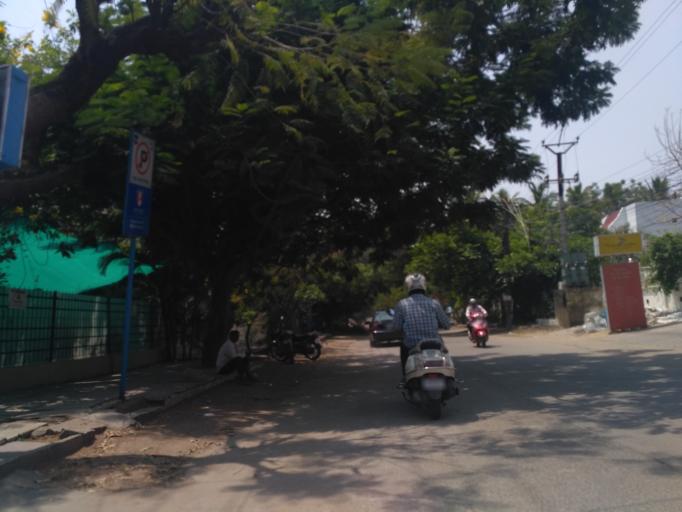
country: IN
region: Telangana
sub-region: Rangareddi
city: Kukatpalli
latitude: 17.4281
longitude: 78.4068
